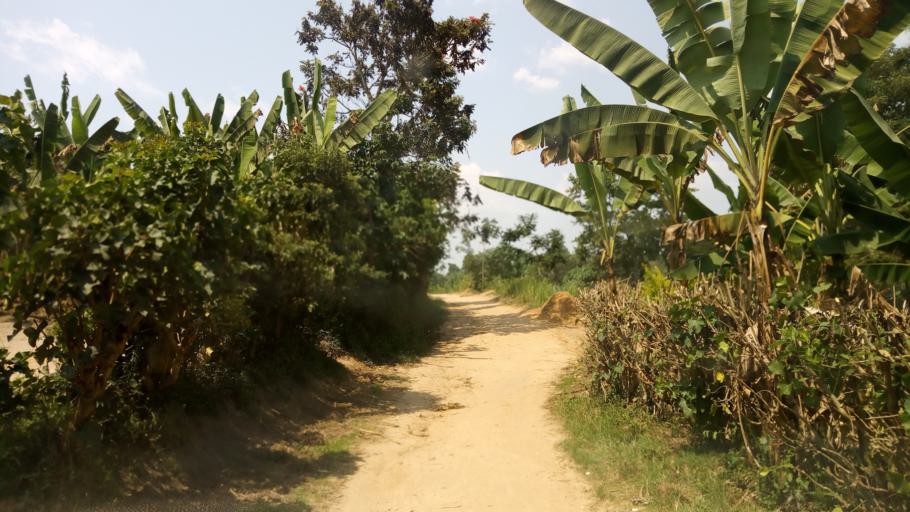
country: UG
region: Western Region
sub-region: Kanungu District
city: Ntungamo
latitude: -0.8060
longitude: 29.6460
